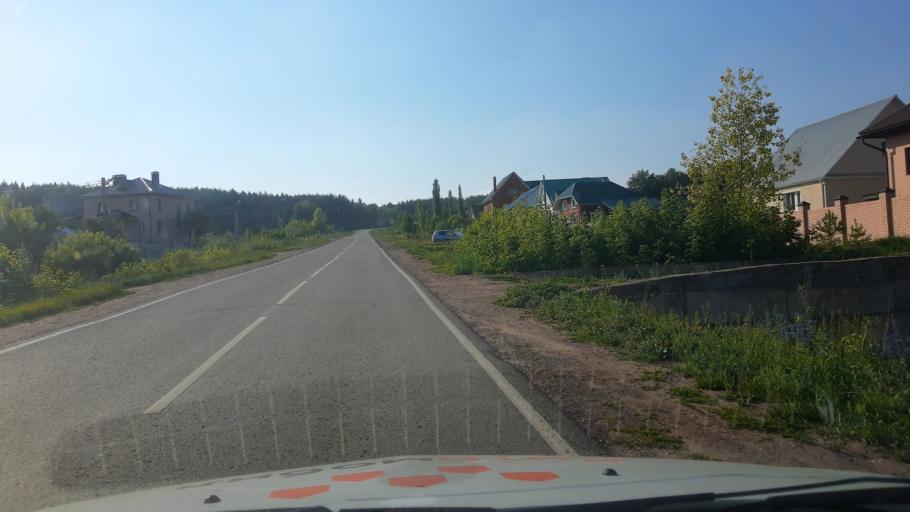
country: RU
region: Bashkortostan
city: Avdon
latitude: 54.6190
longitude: 55.6358
